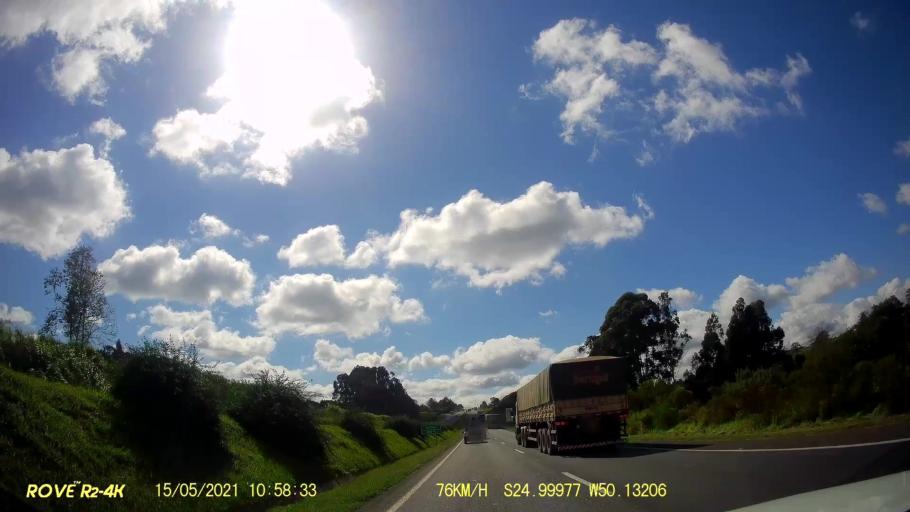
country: BR
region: Parana
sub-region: Carambei
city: Carambei
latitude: -24.9998
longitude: -50.1321
